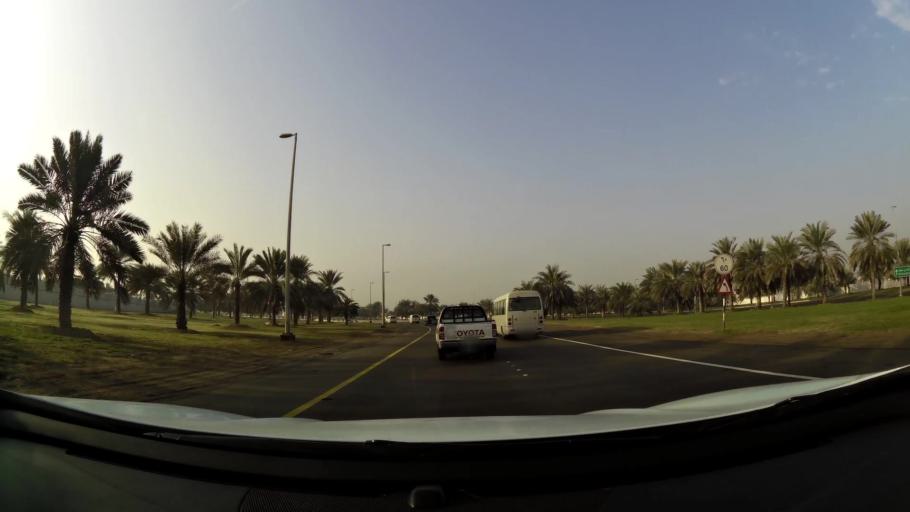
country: AE
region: Abu Dhabi
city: Abu Dhabi
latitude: 24.4214
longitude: 54.4745
